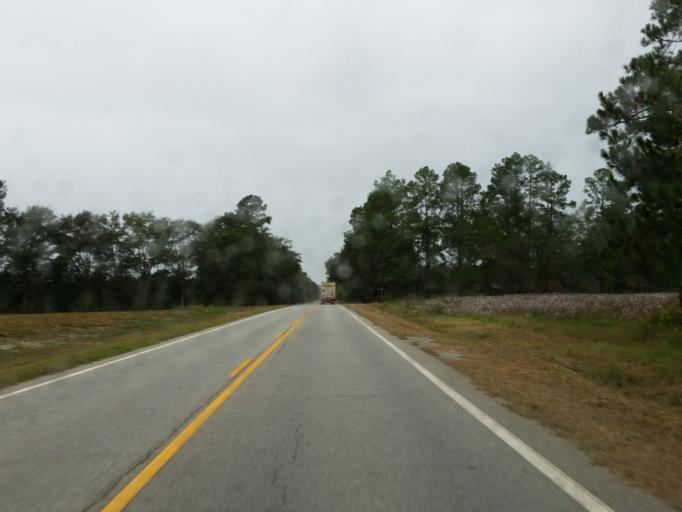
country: US
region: Georgia
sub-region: Berrien County
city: Ray City
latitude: 31.0937
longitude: -83.2564
